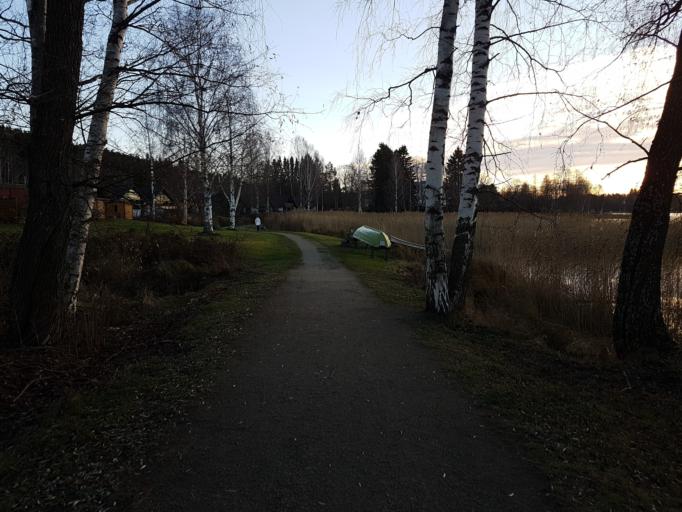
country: FI
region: Northern Savo
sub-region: Kuopio
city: Kuopio
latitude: 62.9358
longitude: 27.6292
